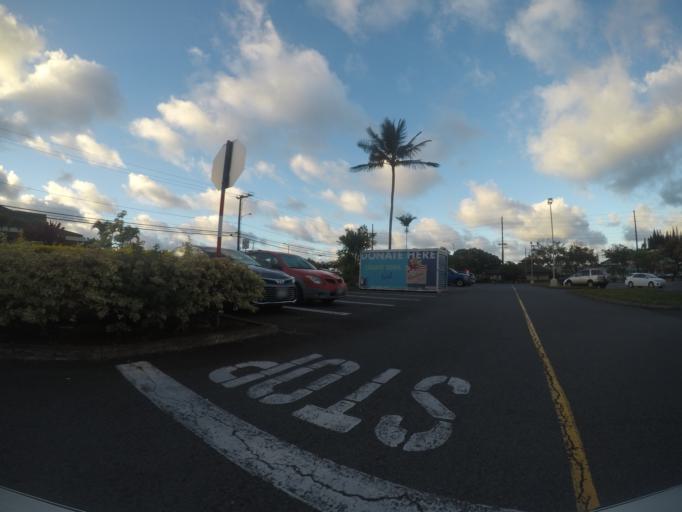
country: US
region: Hawaii
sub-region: Honolulu County
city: He'eia
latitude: 21.4215
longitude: -157.8049
